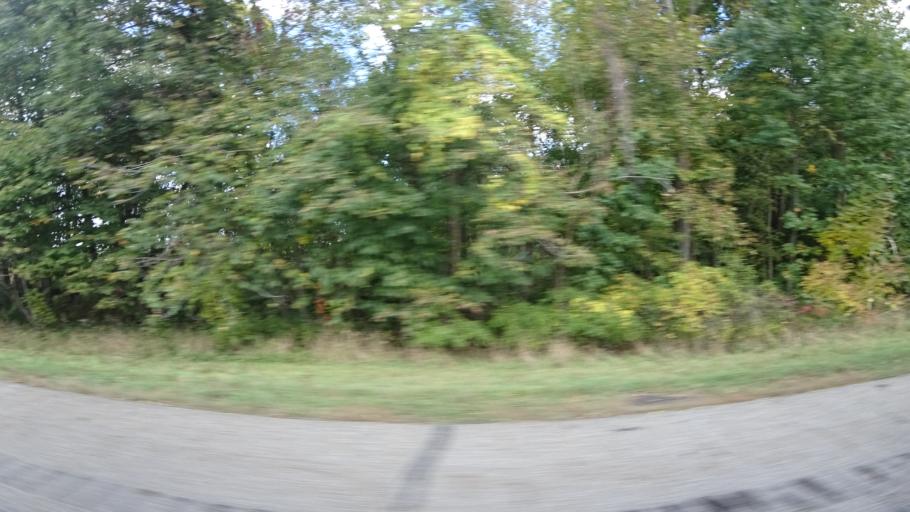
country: US
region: Michigan
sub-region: Branch County
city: Union City
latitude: 42.1059
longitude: -85.0149
